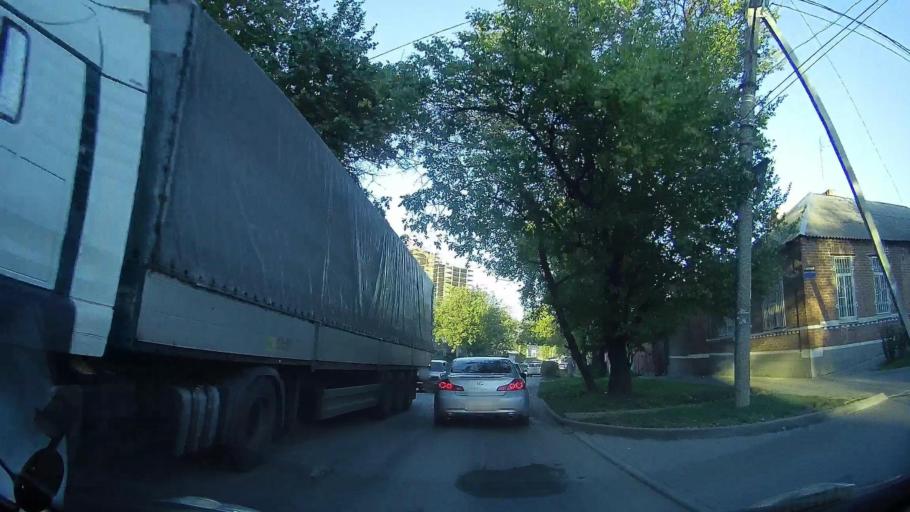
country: RU
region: Rostov
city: Rostov-na-Donu
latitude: 47.2441
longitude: 39.6921
